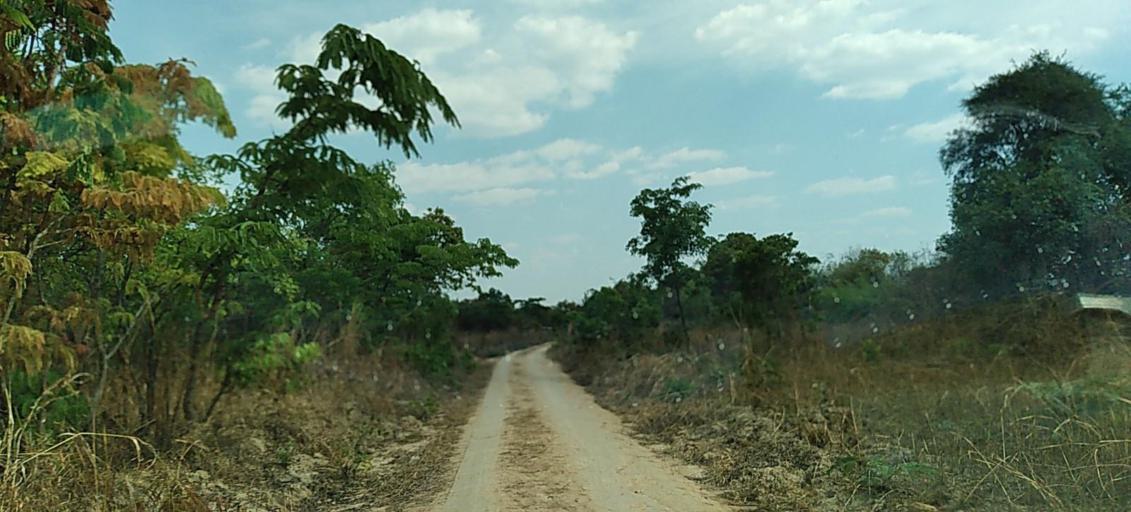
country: ZM
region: Copperbelt
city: Chililabombwe
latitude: -12.3314
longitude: 27.7859
